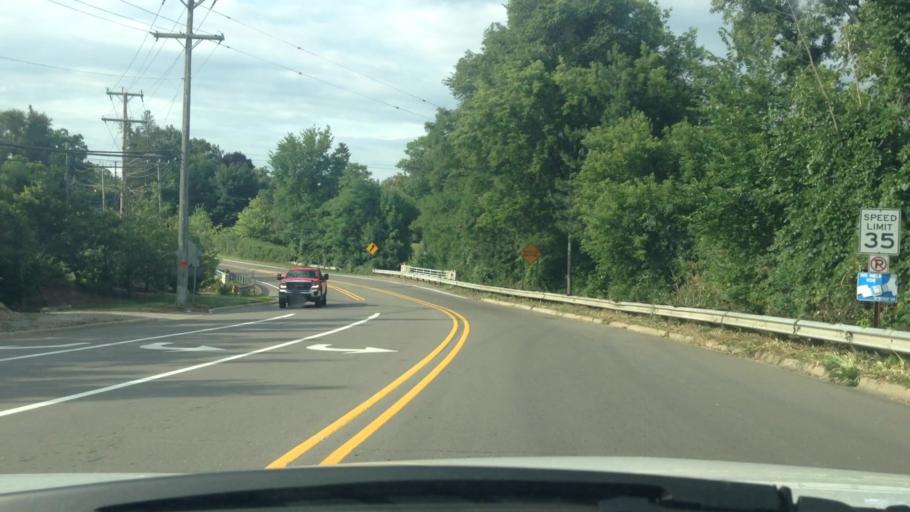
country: US
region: Michigan
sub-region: Oakland County
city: Pontiac
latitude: 42.6790
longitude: -83.3340
